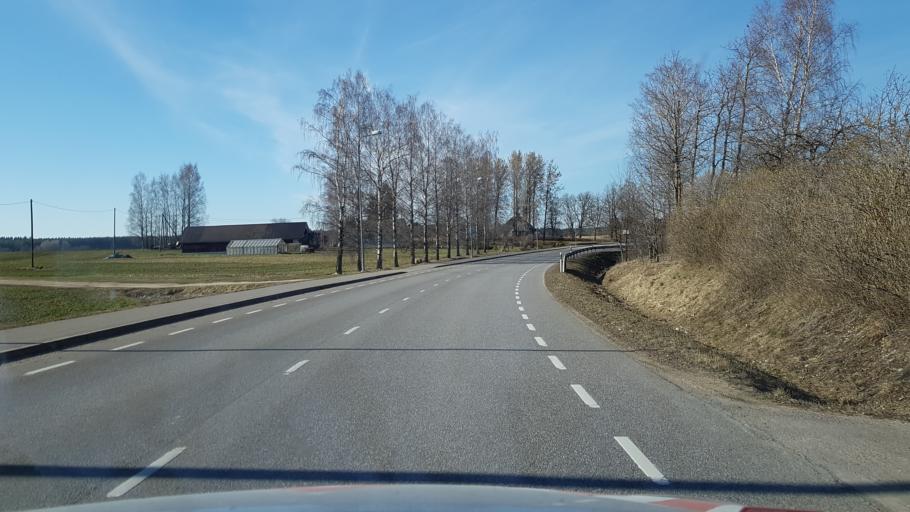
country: EE
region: Laeaene-Virumaa
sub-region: Vinni vald
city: Vinni
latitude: 59.1552
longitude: 26.5891
